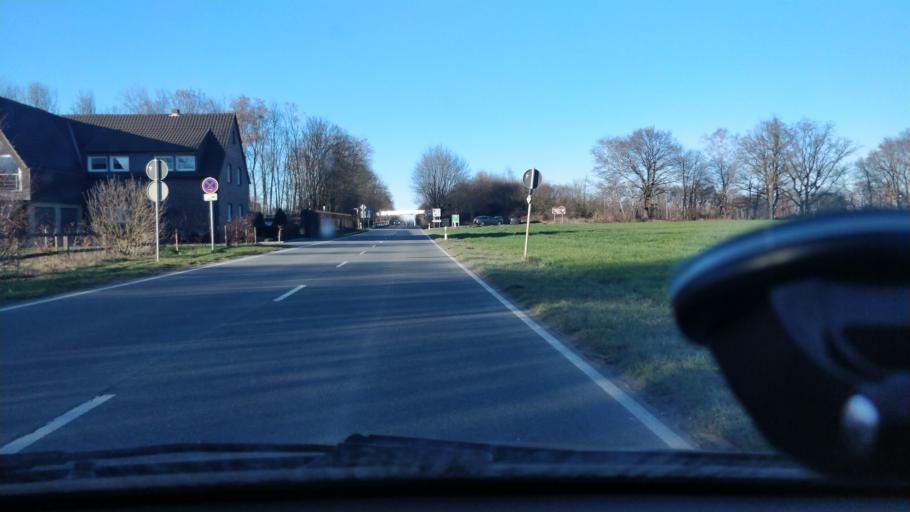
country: DE
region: North Rhine-Westphalia
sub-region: Regierungsbezirk Munster
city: Bottrop
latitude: 51.5989
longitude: 6.8891
